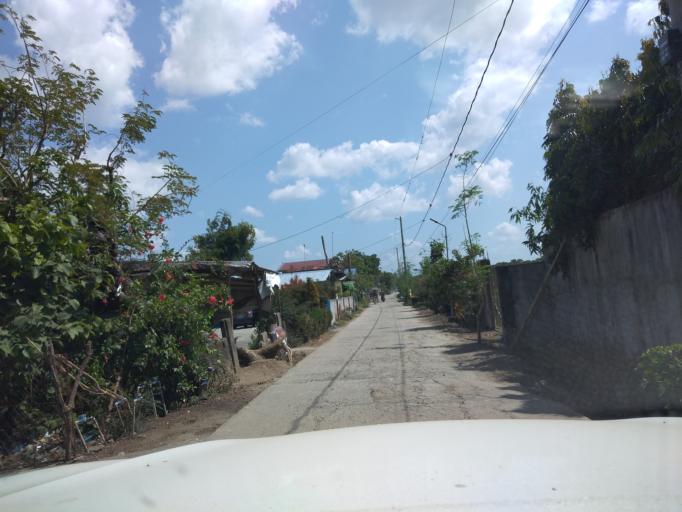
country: PH
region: Central Luzon
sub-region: Province of Pampanga
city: Bahay Pare
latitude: 15.0452
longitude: 120.8841
